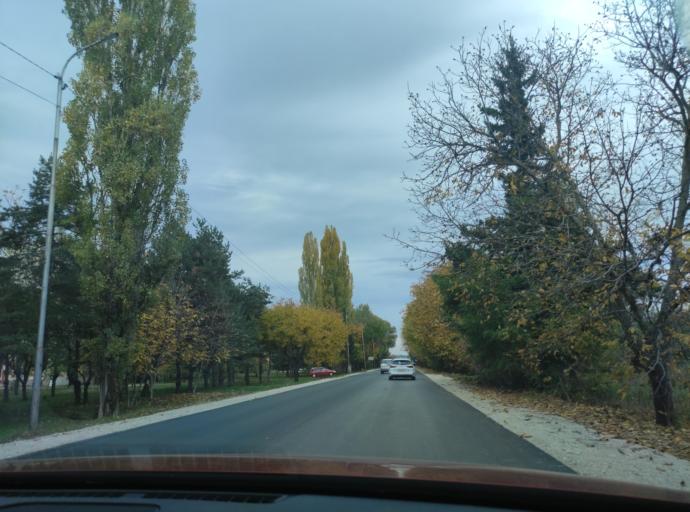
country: BG
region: Montana
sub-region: Obshtina Montana
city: Montana
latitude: 43.3987
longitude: 23.2402
